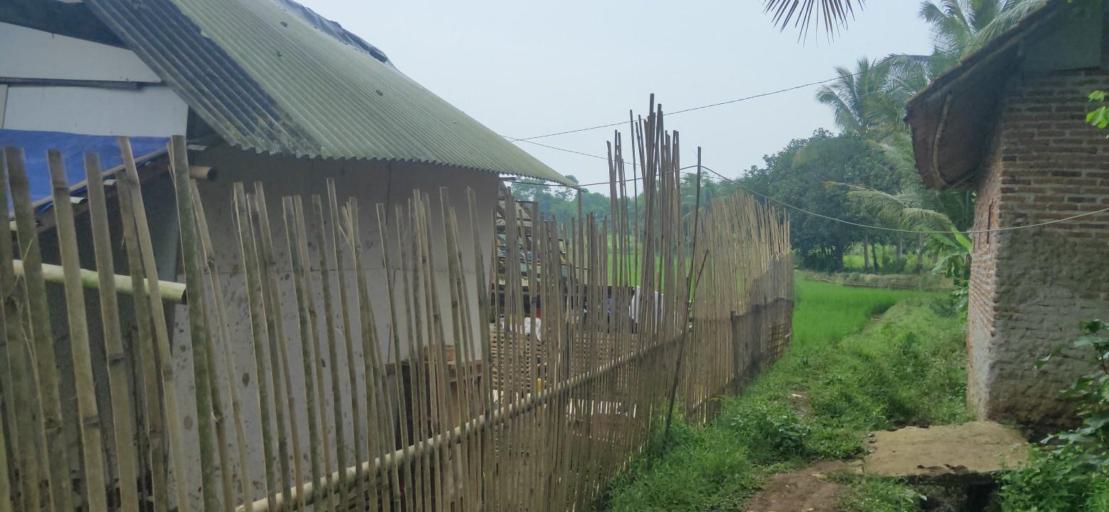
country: ID
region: West Java
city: Pangradin Satu
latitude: -6.4502
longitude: 106.4598
